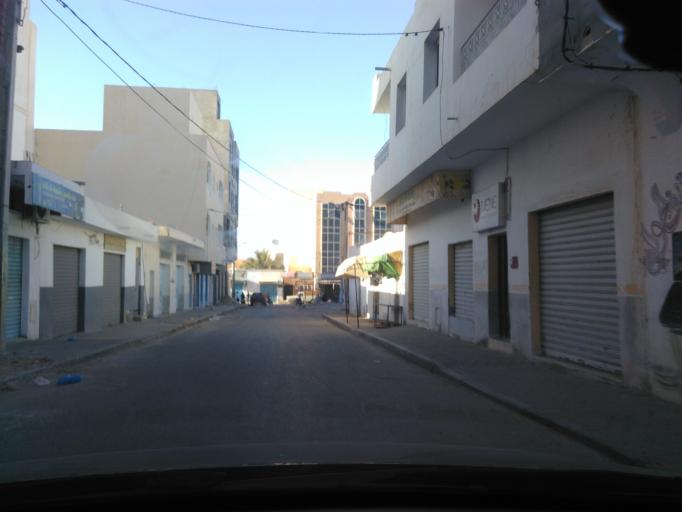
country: TN
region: Tataouine
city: Tataouine
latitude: 32.9275
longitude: 10.4509
